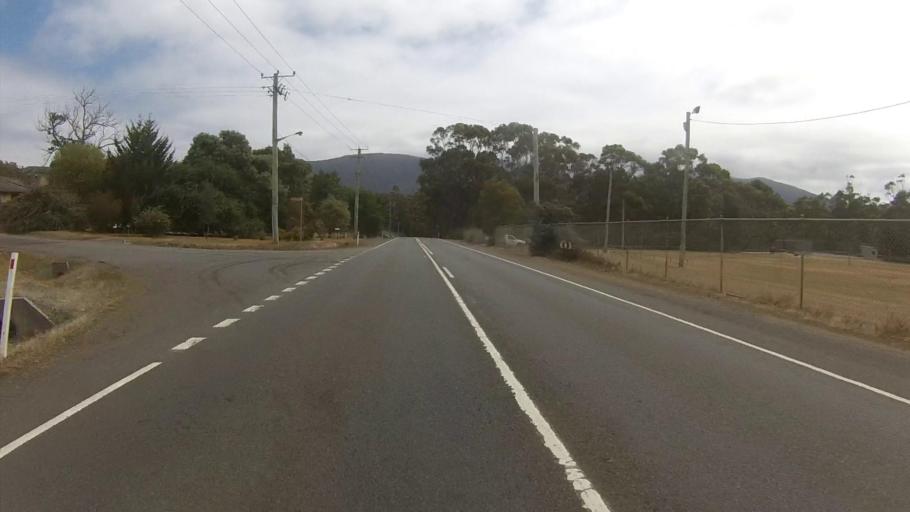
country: AU
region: Tasmania
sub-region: Kingborough
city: Margate
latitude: -42.9893
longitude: 147.1976
